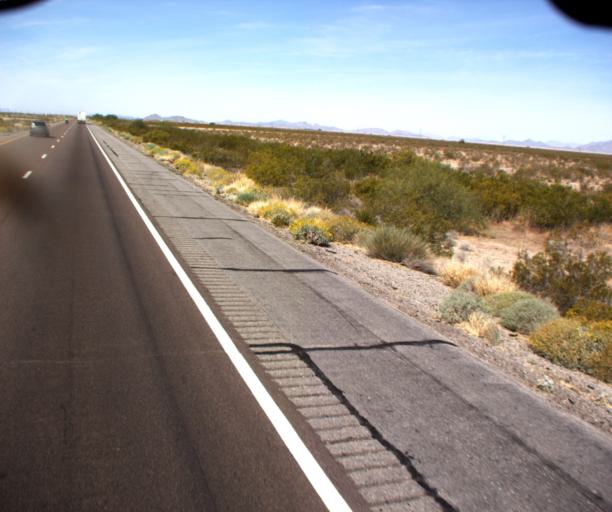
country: US
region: Arizona
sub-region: La Paz County
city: Salome
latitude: 33.5634
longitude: -113.3144
